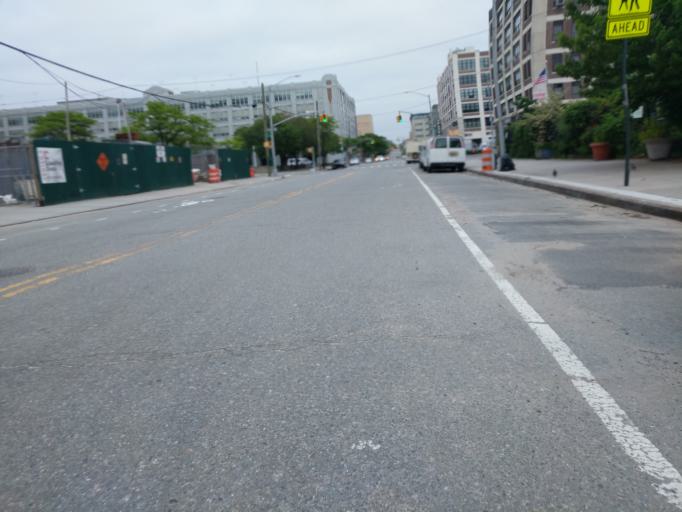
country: US
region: New York
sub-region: Queens County
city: Long Island City
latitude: 40.7433
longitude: -73.9384
